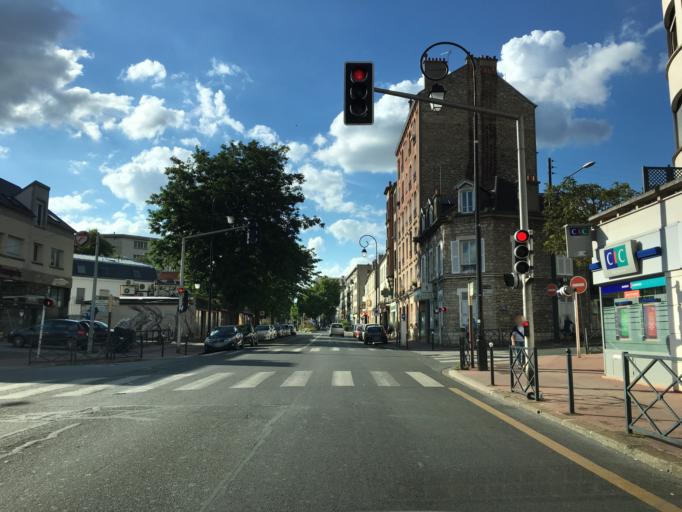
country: FR
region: Ile-de-France
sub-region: Departement du Val-de-Marne
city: Joinville-le-Pont
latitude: 48.8089
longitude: 2.4724
